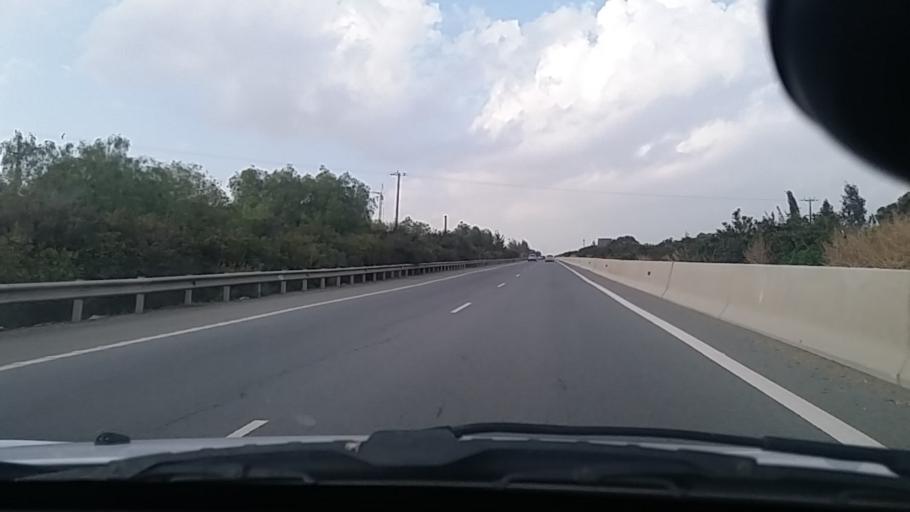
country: CY
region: Lefkosia
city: Kato Deftera
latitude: 35.1343
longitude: 33.2839
